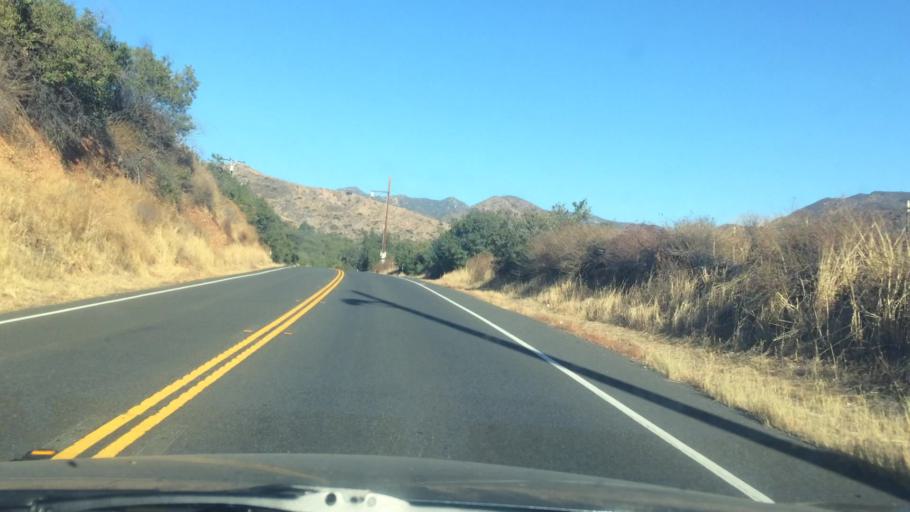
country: US
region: California
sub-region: Orange County
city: Coto De Caza
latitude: 33.5761
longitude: -117.5386
